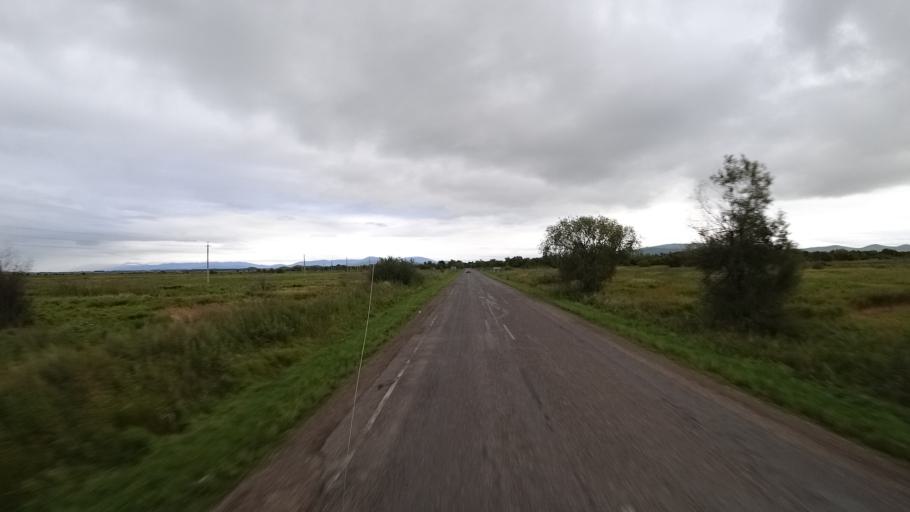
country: RU
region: Primorskiy
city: Chernigovka
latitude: 44.3578
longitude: 132.5598
